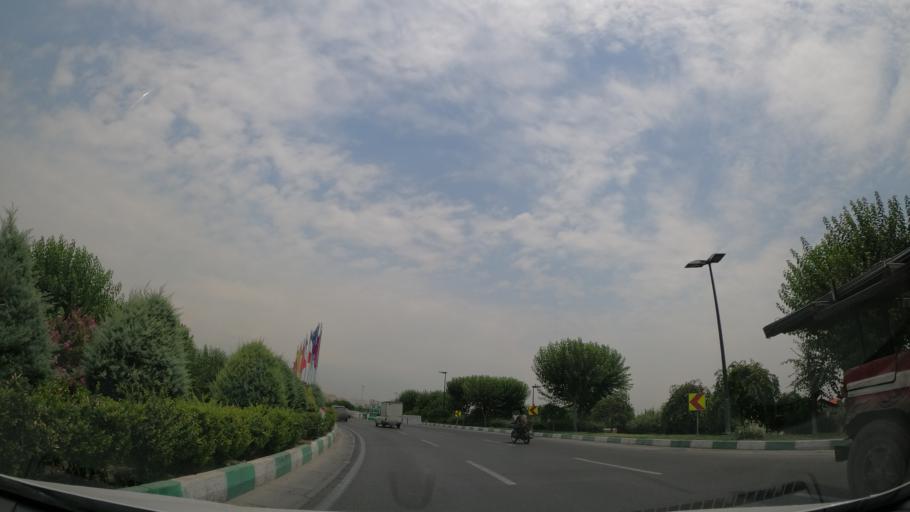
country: IR
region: Tehran
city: Tehran
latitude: 35.6788
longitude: 51.3412
